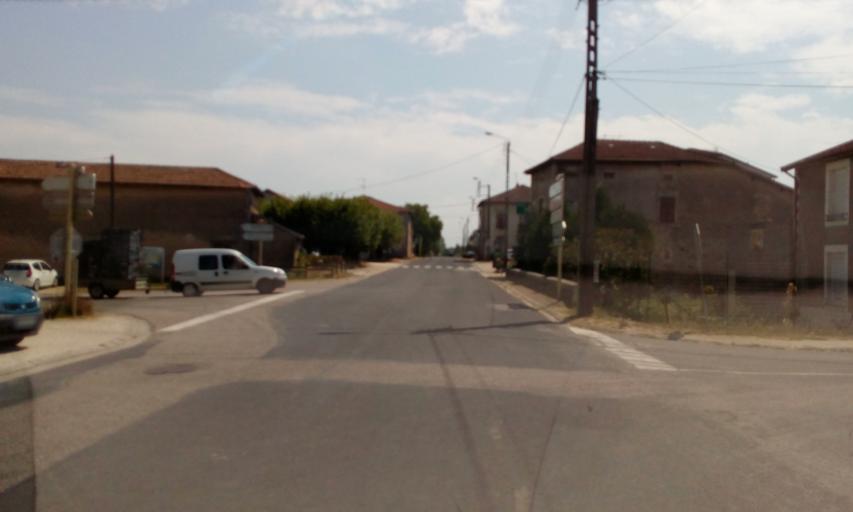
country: FR
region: Lorraine
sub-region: Departement de la Meuse
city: Vigneulles-les-Hattonchatel
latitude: 49.0390
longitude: 5.6573
